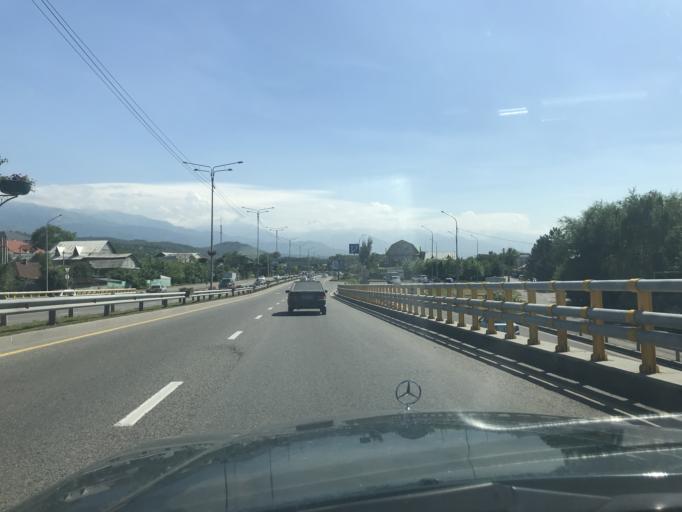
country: KZ
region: Almaty Qalasy
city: Almaty
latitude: 43.2825
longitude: 76.9864
